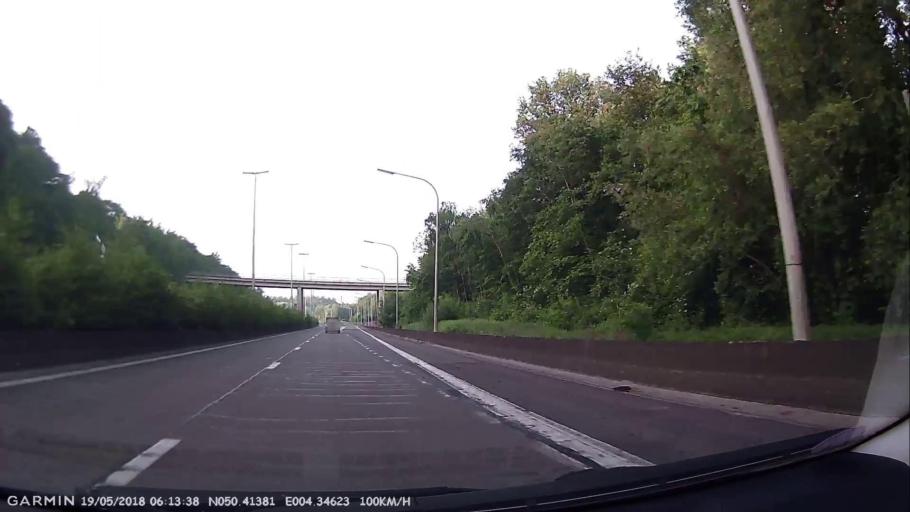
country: BE
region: Wallonia
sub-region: Province du Hainaut
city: Courcelles
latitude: 50.4135
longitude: 4.3462
